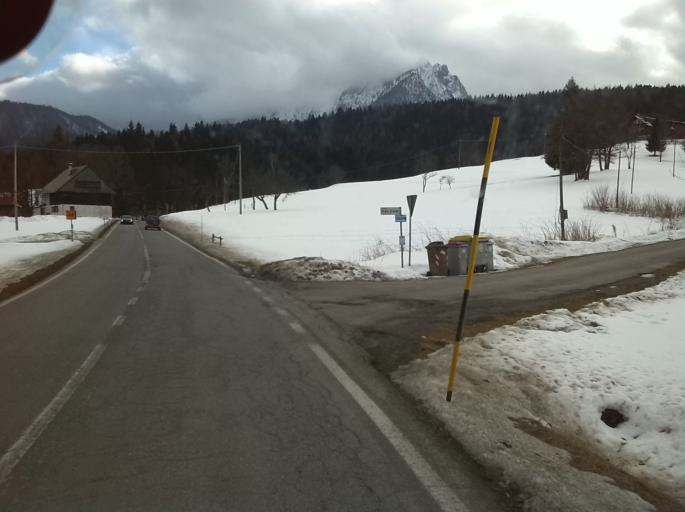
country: IT
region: Friuli Venezia Giulia
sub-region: Provincia di Udine
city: Tarvisio
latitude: 46.5062
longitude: 13.6141
